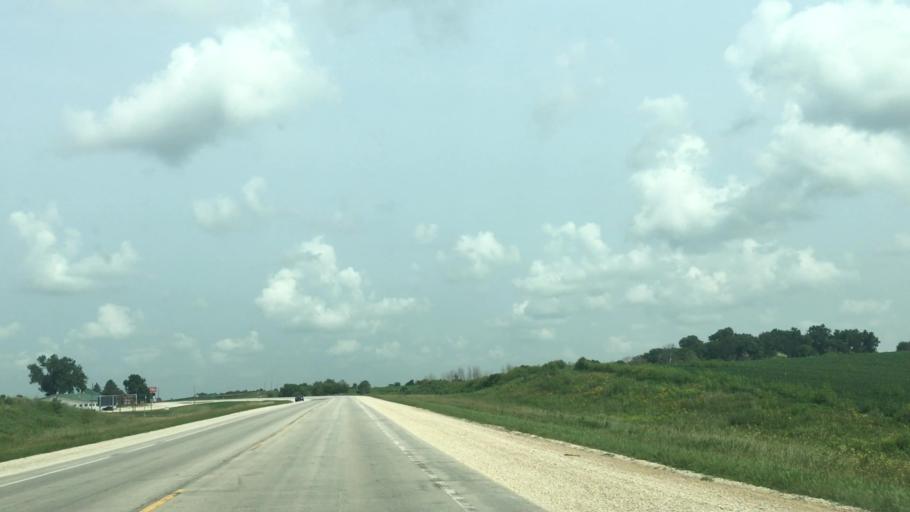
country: US
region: Iowa
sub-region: Winneshiek County
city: Decorah
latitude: 43.3607
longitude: -91.8043
